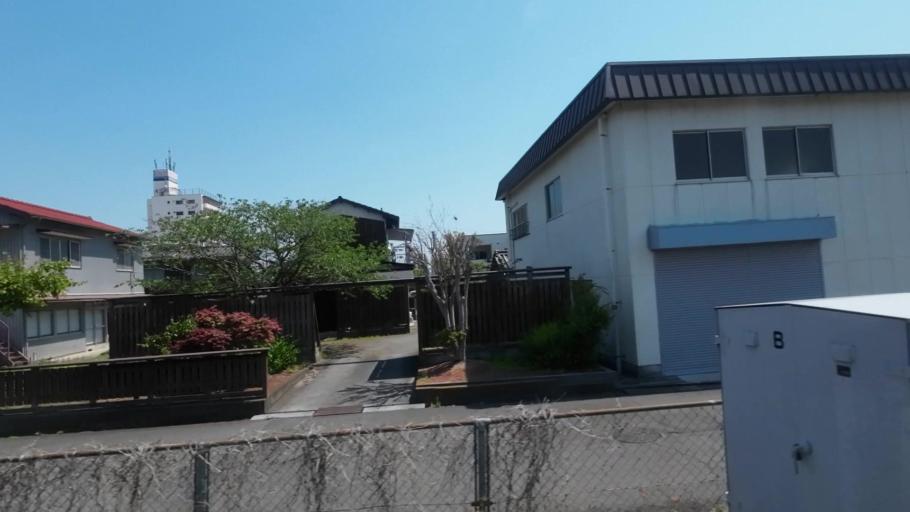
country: JP
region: Ehime
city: Saijo
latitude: 33.9286
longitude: 133.0865
